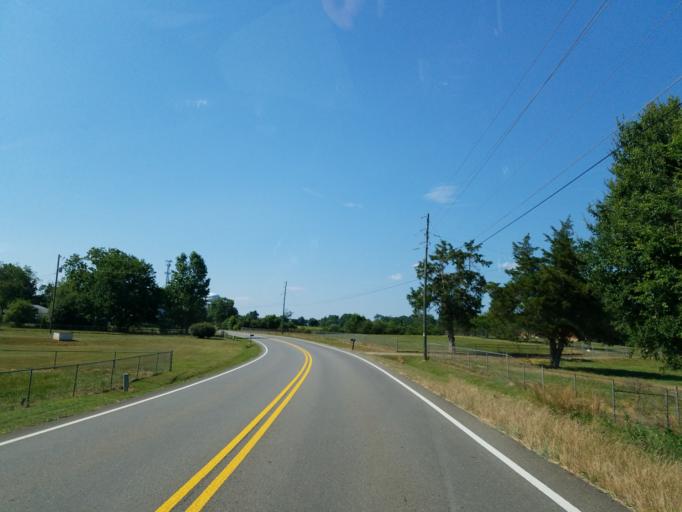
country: US
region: Georgia
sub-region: Fulton County
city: Milton
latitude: 34.2298
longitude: -84.2898
